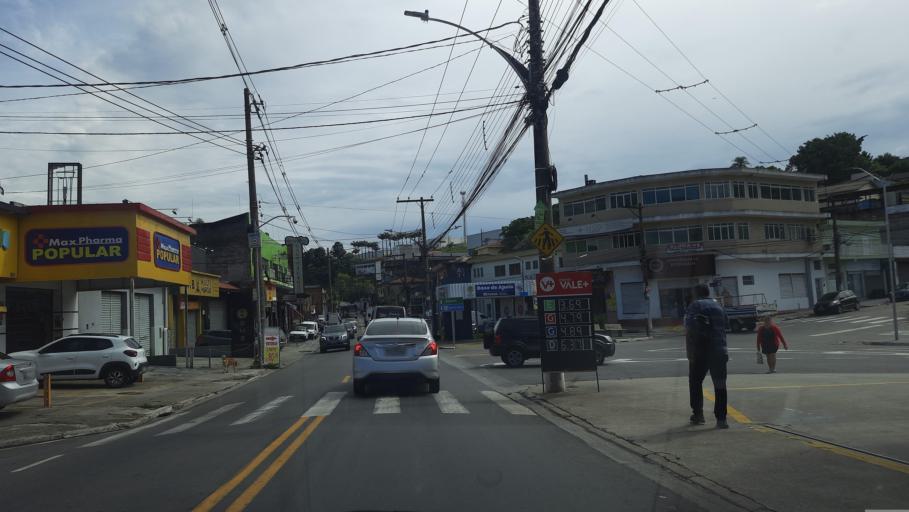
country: BR
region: Sao Paulo
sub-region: Caieiras
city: Caieiras
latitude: -23.3909
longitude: -46.7146
